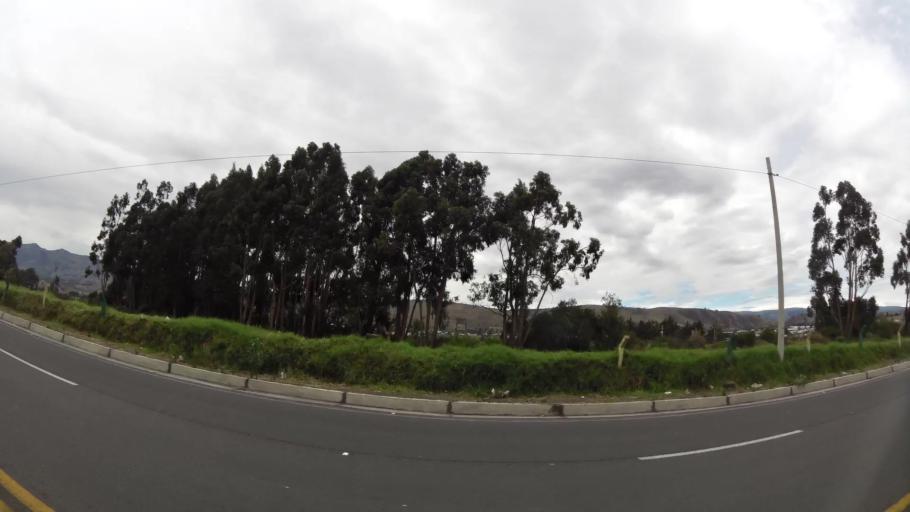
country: EC
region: Cotopaxi
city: San Miguel de Salcedo
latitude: -1.0195
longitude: -78.5920
